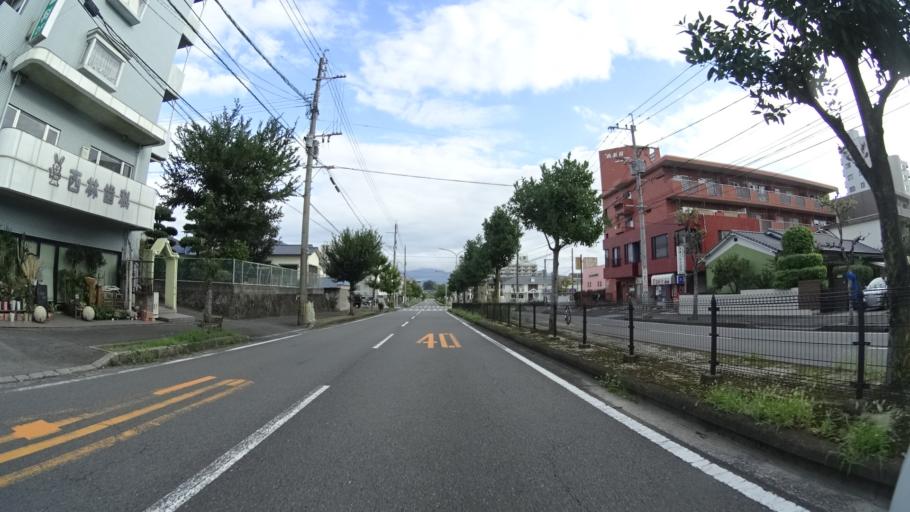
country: JP
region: Oita
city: Beppu
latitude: 33.3016
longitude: 131.4950
